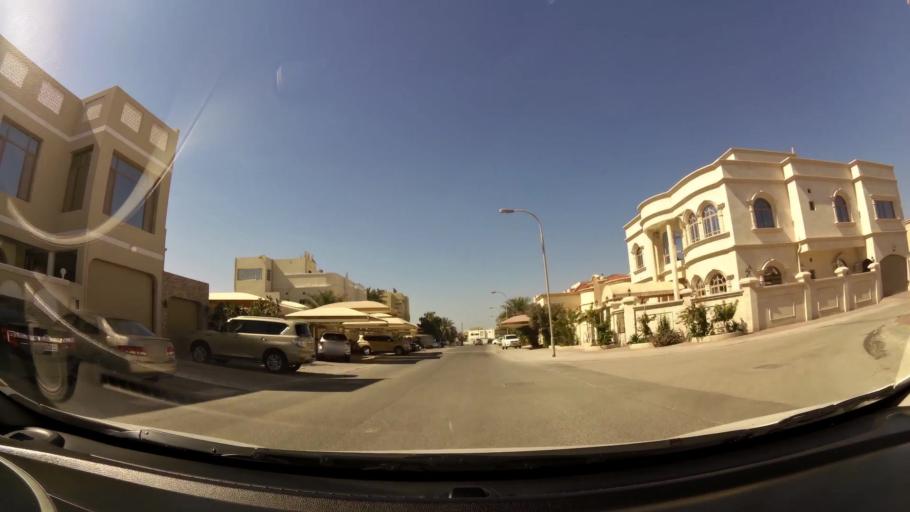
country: BH
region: Muharraq
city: Al Hadd
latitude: 26.2447
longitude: 50.6331
